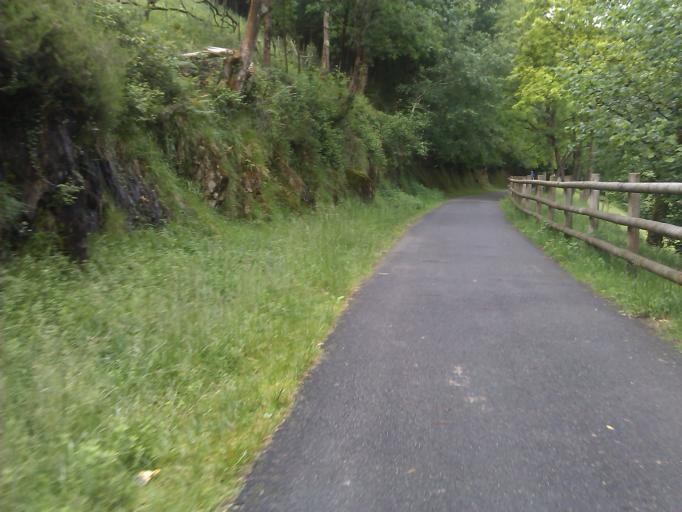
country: ES
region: Basque Country
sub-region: Provincia de Guipuzcoa
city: Andoain
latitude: 43.2087
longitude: -2.0113
